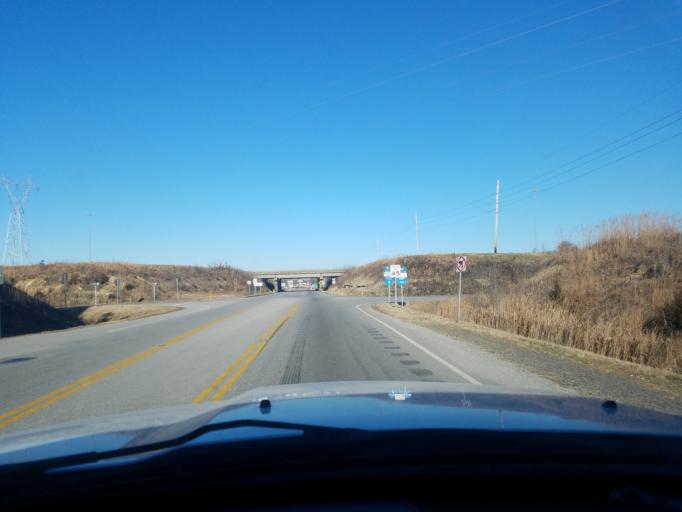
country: US
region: Kentucky
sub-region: Ohio County
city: Beaver Dam
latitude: 37.3665
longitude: -86.8412
